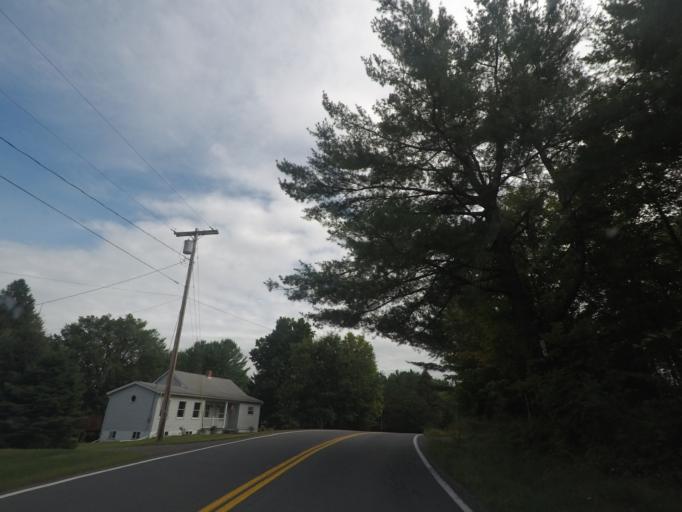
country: US
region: New York
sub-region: Rensselaer County
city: Nassau
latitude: 42.5447
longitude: -73.6092
